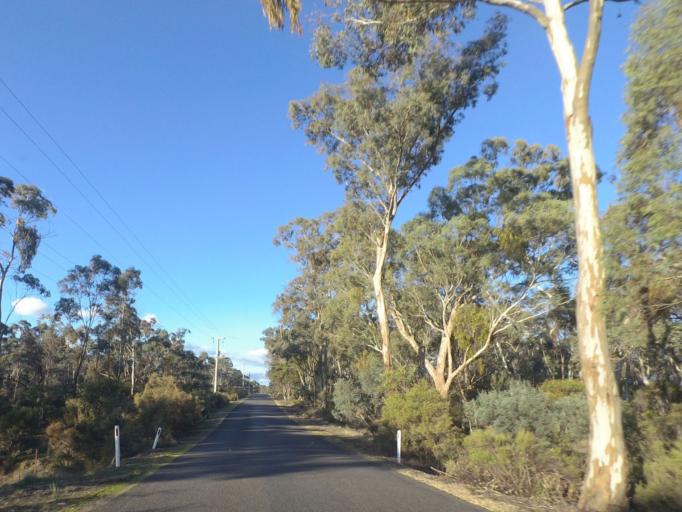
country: AU
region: Victoria
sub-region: Mount Alexander
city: Castlemaine
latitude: -37.1432
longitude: 144.1906
